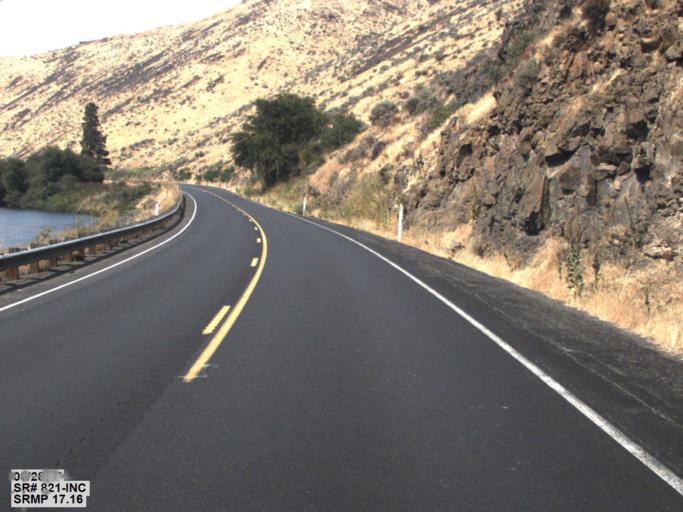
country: US
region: Washington
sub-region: Kittitas County
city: Kittitas
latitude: 46.8656
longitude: -120.4786
